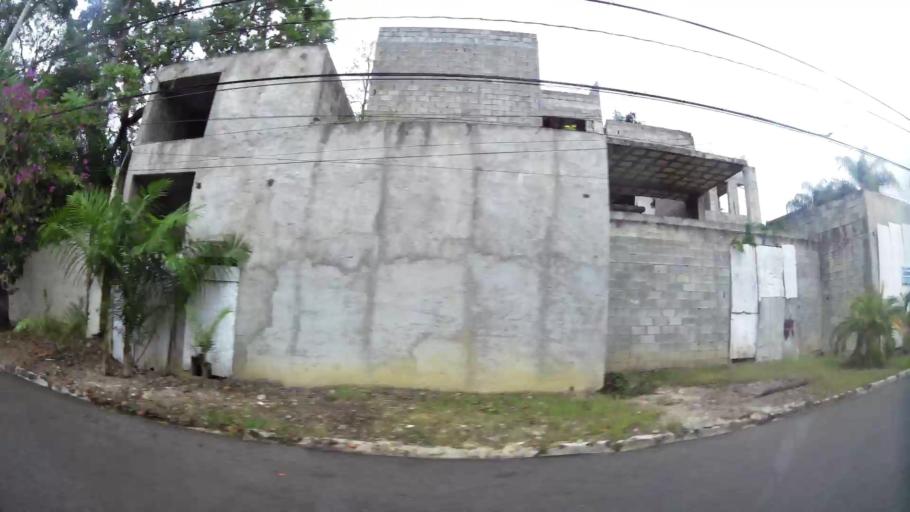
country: DO
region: Nacional
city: La Agustina
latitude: 18.5113
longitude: -69.9521
